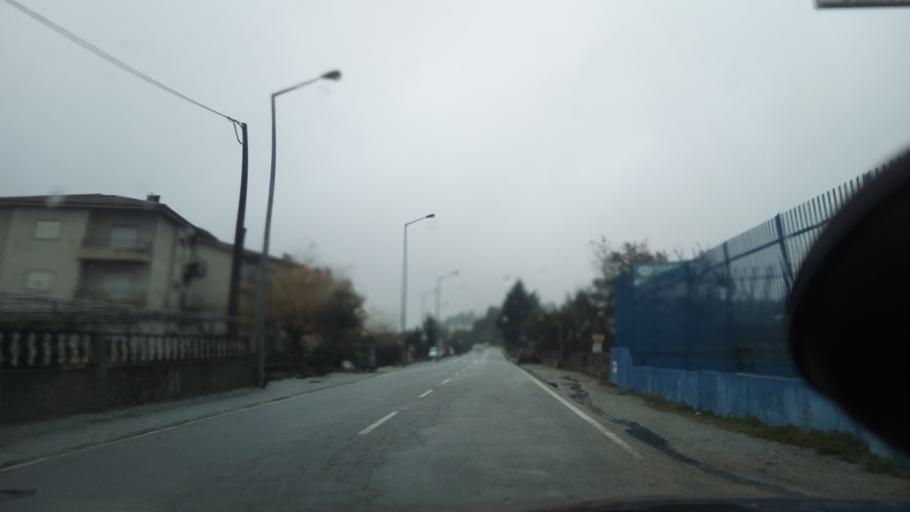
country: PT
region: Viseu
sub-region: Mangualde
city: Mangualde
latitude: 40.6053
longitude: -7.7783
